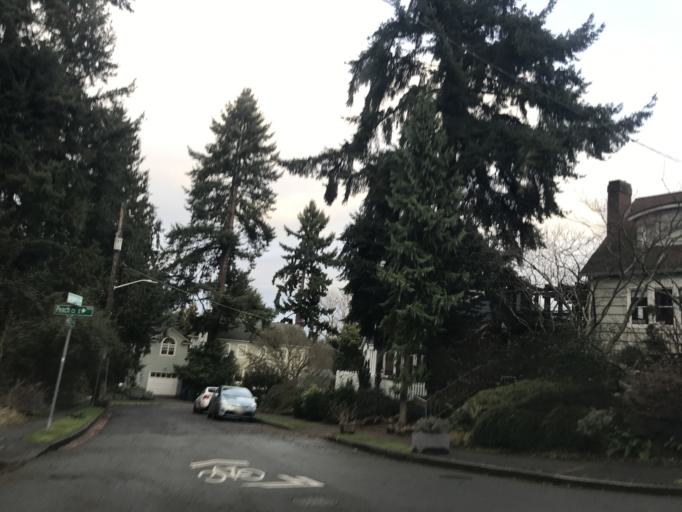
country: US
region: Washington
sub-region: King County
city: Seattle
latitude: 47.6346
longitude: -122.3055
